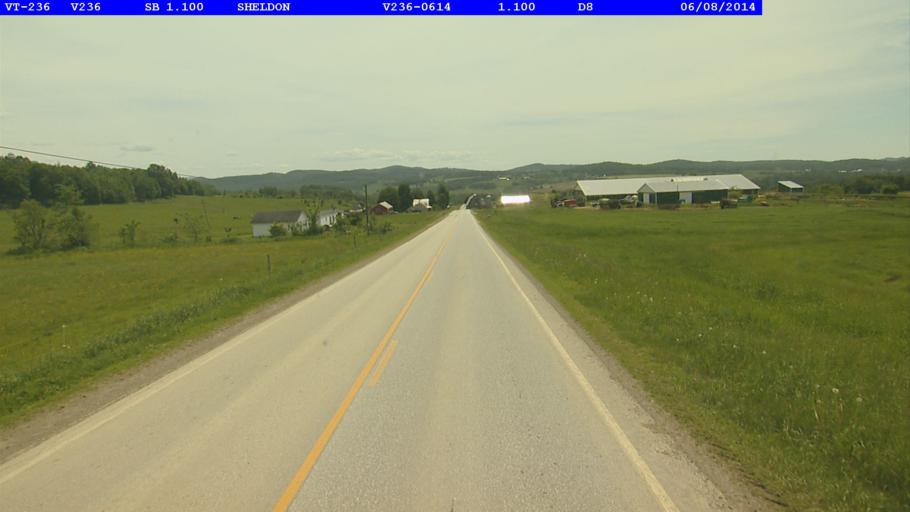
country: US
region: Vermont
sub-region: Franklin County
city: Enosburg Falls
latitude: 44.9267
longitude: -72.8658
